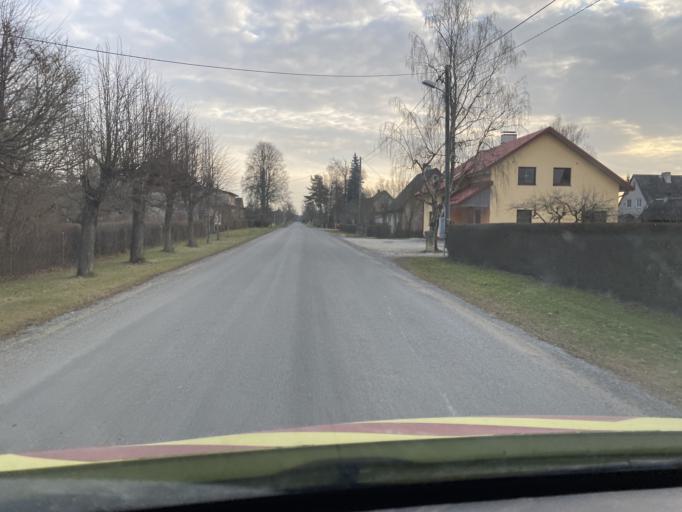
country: EE
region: Jogevamaa
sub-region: Poltsamaa linn
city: Poltsamaa
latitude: 58.6514
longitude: 25.9625
